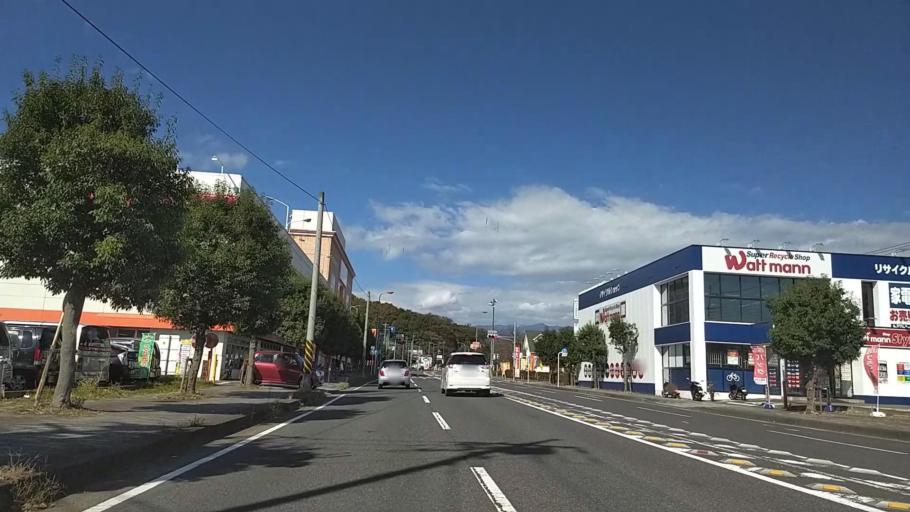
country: JP
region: Kanagawa
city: Ninomiya
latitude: 35.3143
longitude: 139.2437
